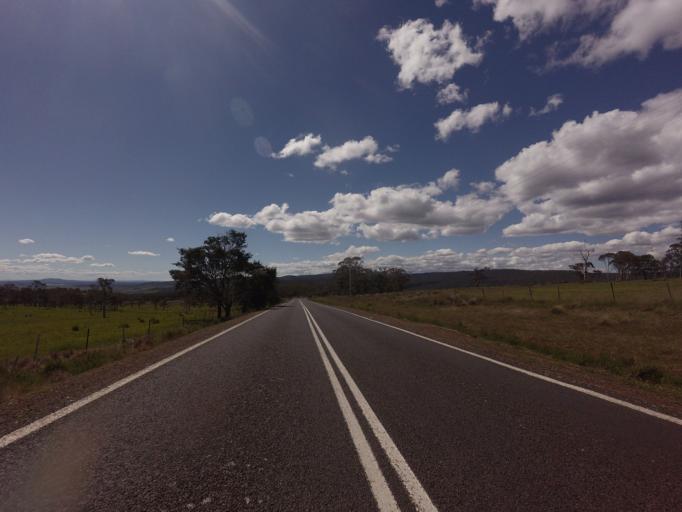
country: AU
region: Tasmania
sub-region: Northern Midlands
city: Evandale
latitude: -41.9462
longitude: 147.6048
